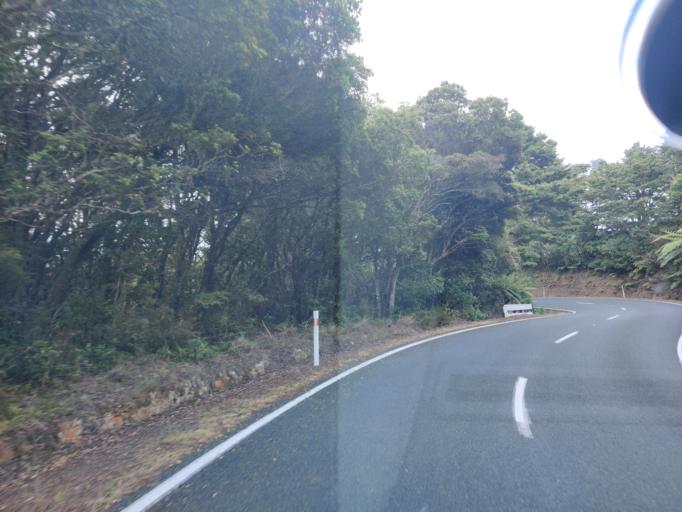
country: NZ
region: Northland
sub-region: Whangarei
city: Ngunguru
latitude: -35.5776
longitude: 174.4092
